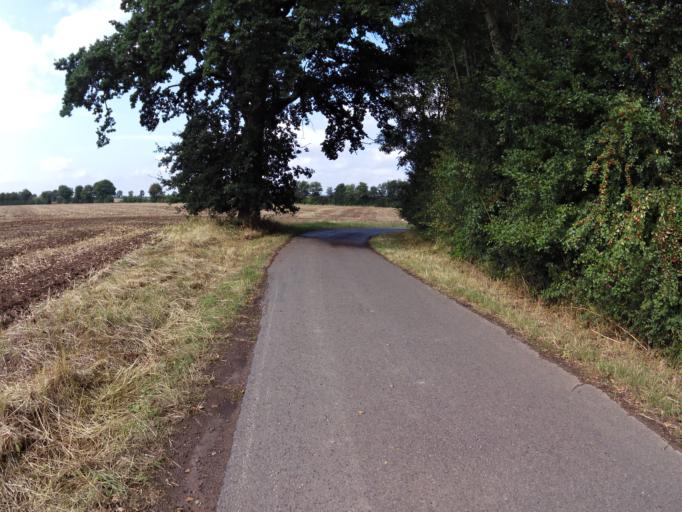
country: DE
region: Lower Saxony
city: Schweringen
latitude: 52.7718
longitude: 9.1716
